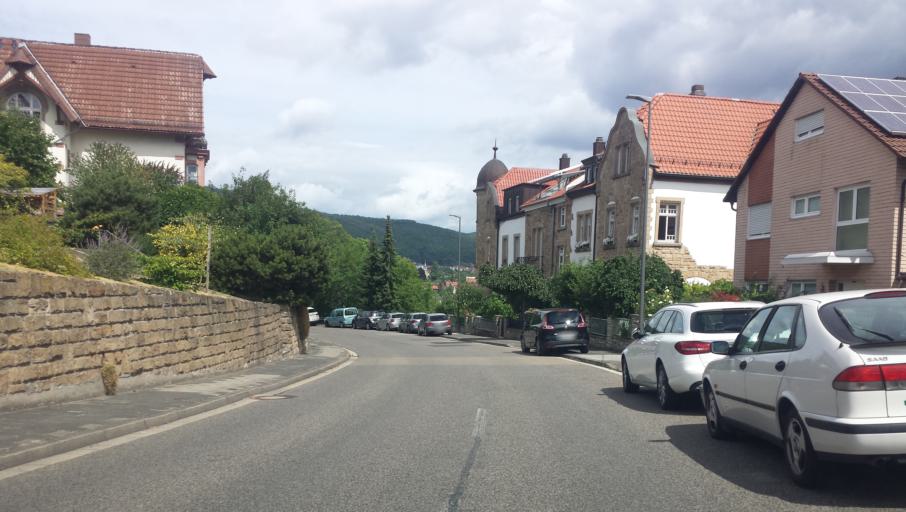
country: DE
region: Rheinland-Pfalz
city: Neustadt
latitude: 49.3478
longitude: 8.1453
